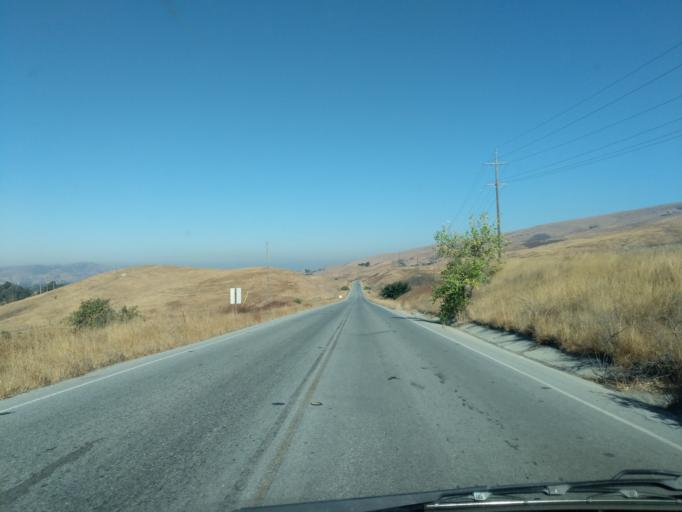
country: US
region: California
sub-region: Santa Clara County
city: Morgan Hill
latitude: 37.1847
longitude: -121.6815
